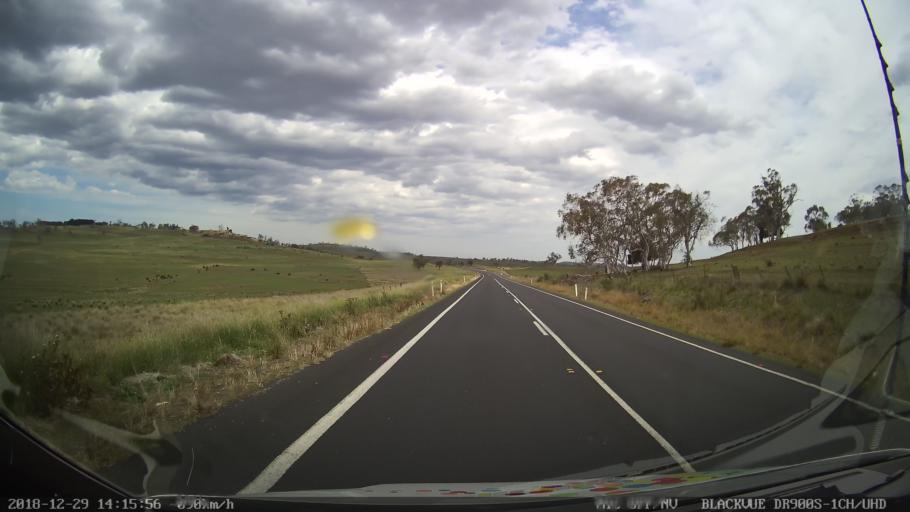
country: AU
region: New South Wales
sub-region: Cooma-Monaro
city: Cooma
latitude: -36.4616
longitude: 149.2449
